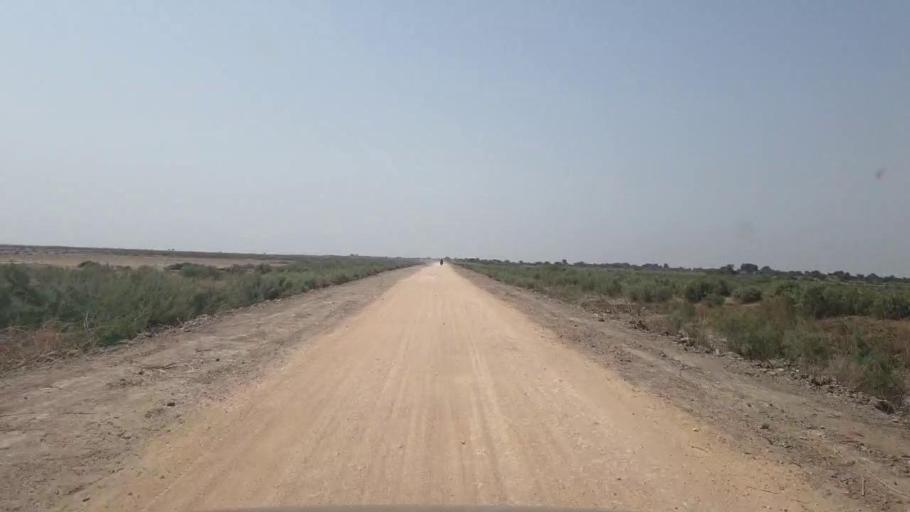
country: PK
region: Sindh
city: Jati
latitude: 24.3712
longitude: 68.5643
